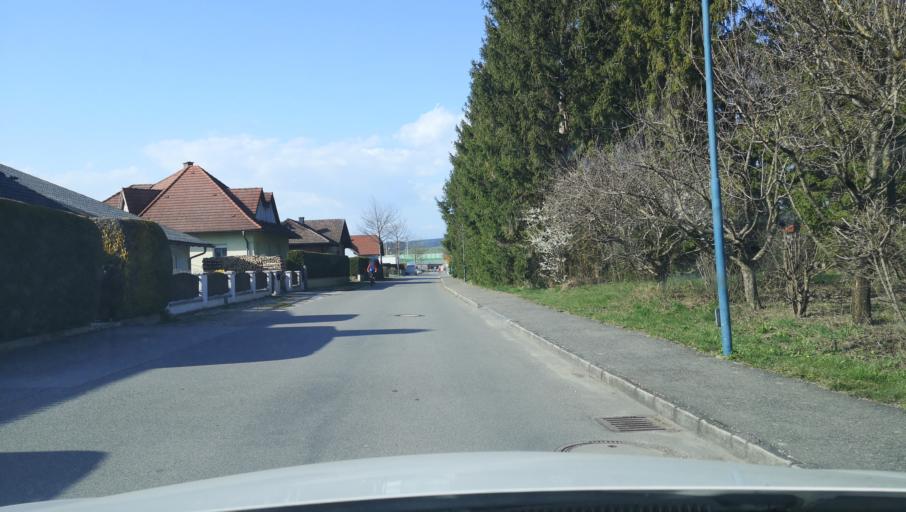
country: AT
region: Lower Austria
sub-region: Politischer Bezirk Melk
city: Blindenmarkt
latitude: 48.1224
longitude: 14.9880
